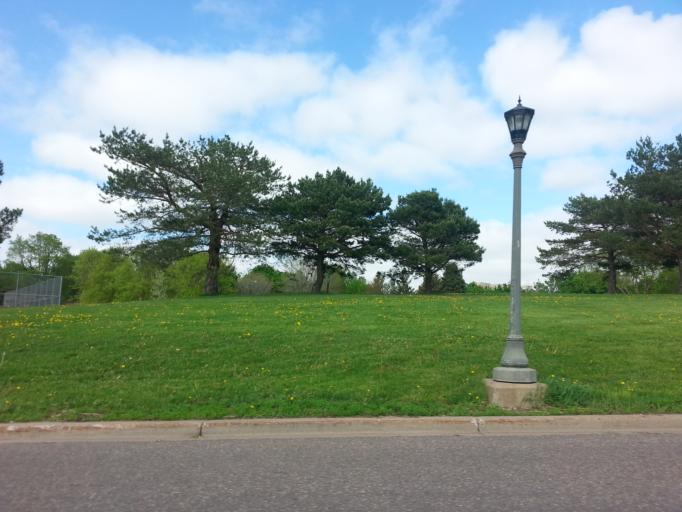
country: US
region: Minnesota
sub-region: Ramsey County
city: Saint Paul
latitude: 44.9463
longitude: -93.0572
